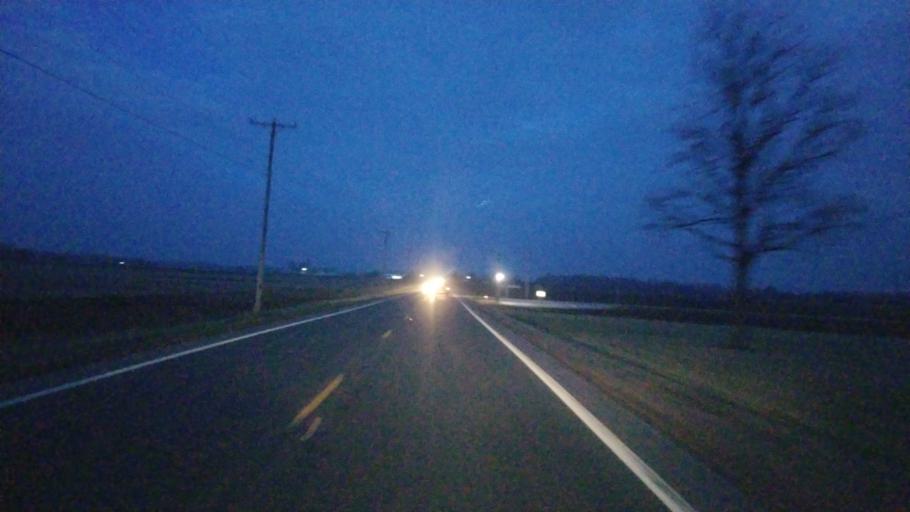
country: US
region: Ohio
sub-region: Auglaize County
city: Wapakoneta
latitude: 40.5558
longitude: -84.1360
